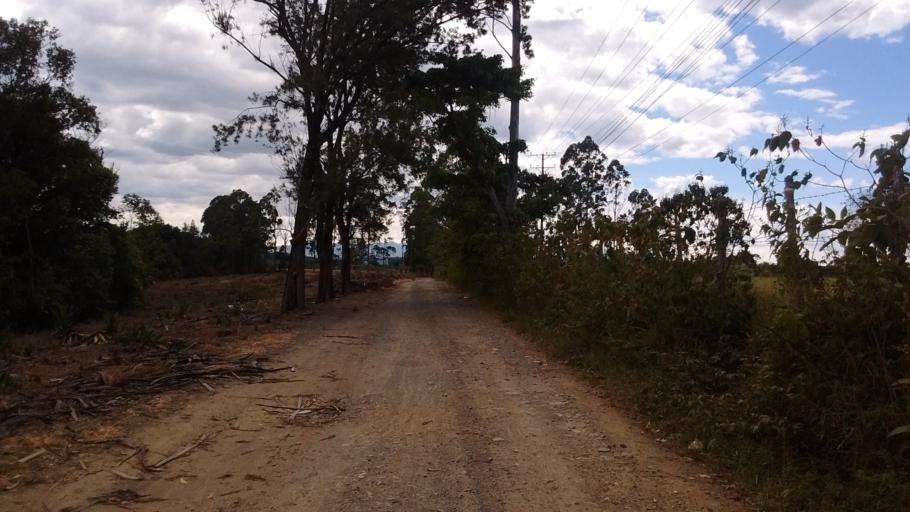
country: CO
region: Cauca
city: Popayan
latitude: 2.4944
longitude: -76.5892
